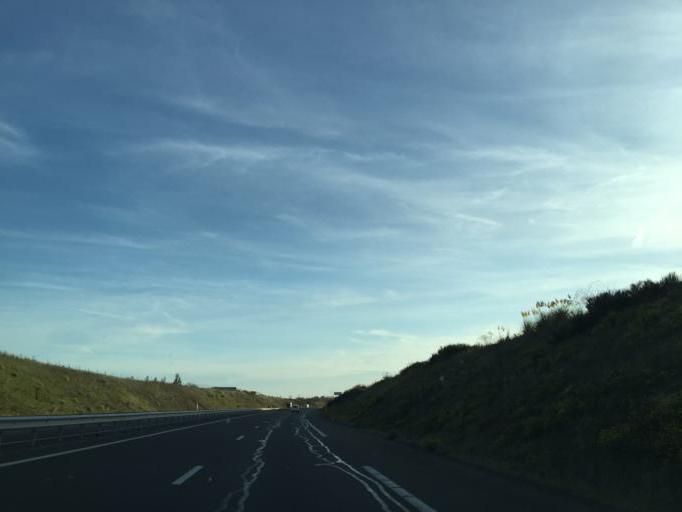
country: FR
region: Rhone-Alpes
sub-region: Departement de l'Isere
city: Satolas-et-Bonce
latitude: 45.7135
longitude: 5.0987
